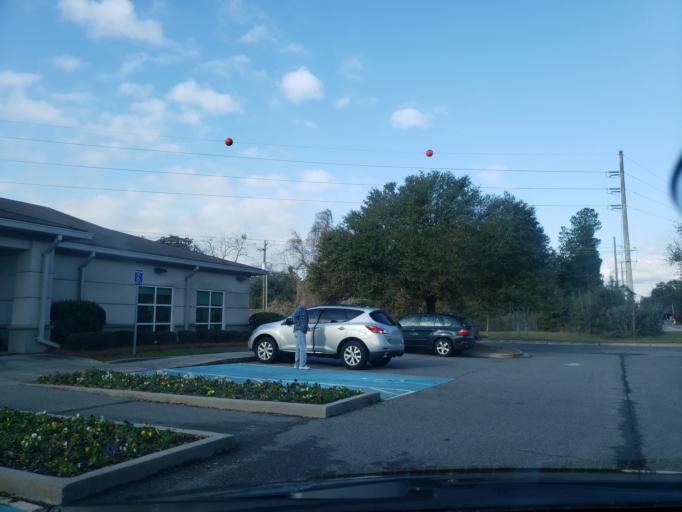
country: US
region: Georgia
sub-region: Chatham County
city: Thunderbolt
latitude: 32.0274
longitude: -81.0875
